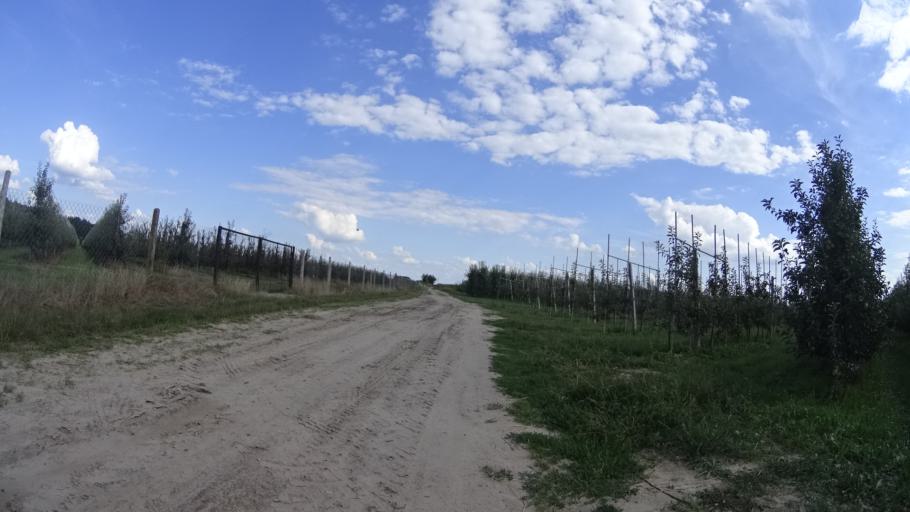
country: PL
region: Masovian Voivodeship
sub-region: Powiat bialobrzeski
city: Wysmierzyce
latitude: 51.6715
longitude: 20.8004
